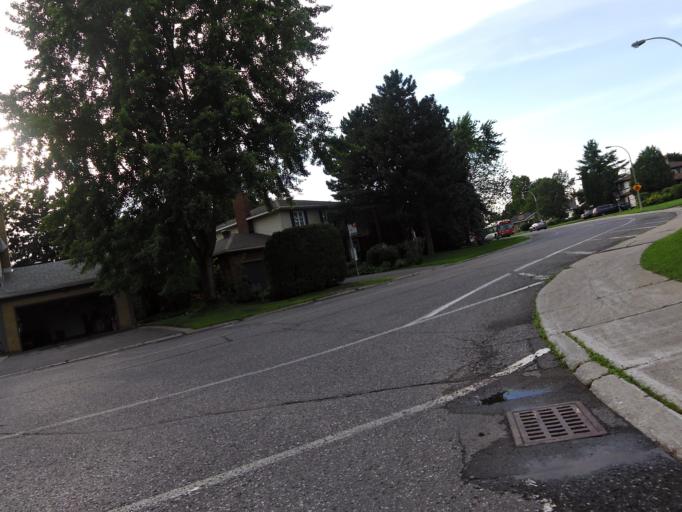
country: CA
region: Ontario
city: Bells Corners
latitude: 45.3238
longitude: -75.7823
